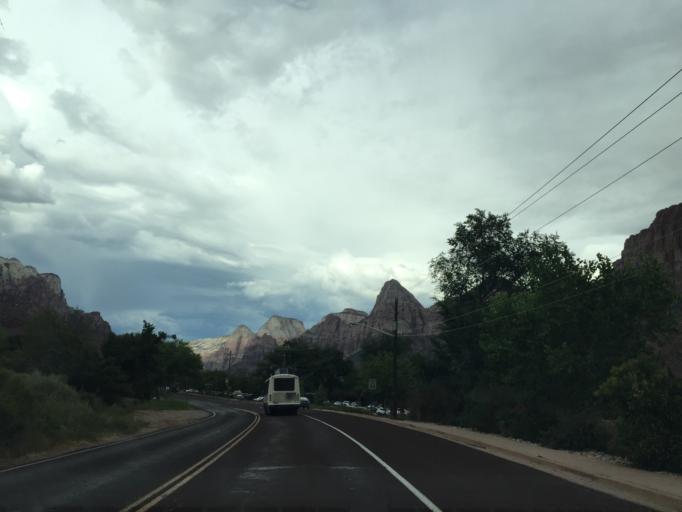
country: US
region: Utah
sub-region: Washington County
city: Hildale
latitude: 37.1824
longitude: -113.0044
